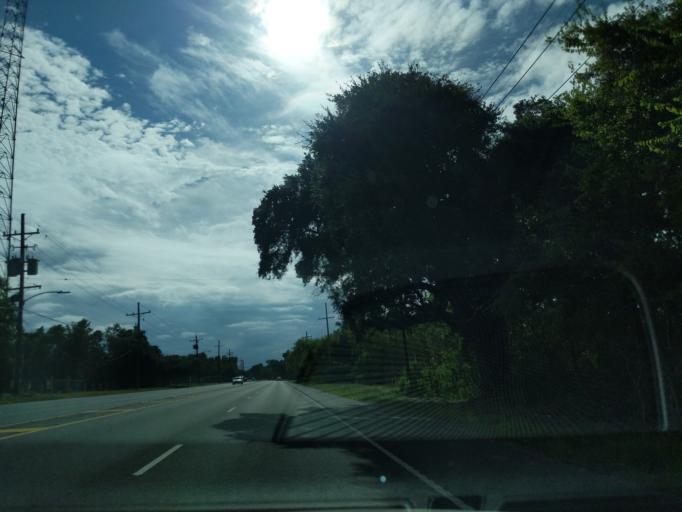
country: US
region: Louisiana
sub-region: Saint Bernard Parish
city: Chalmette
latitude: 30.0481
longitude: -89.8872
